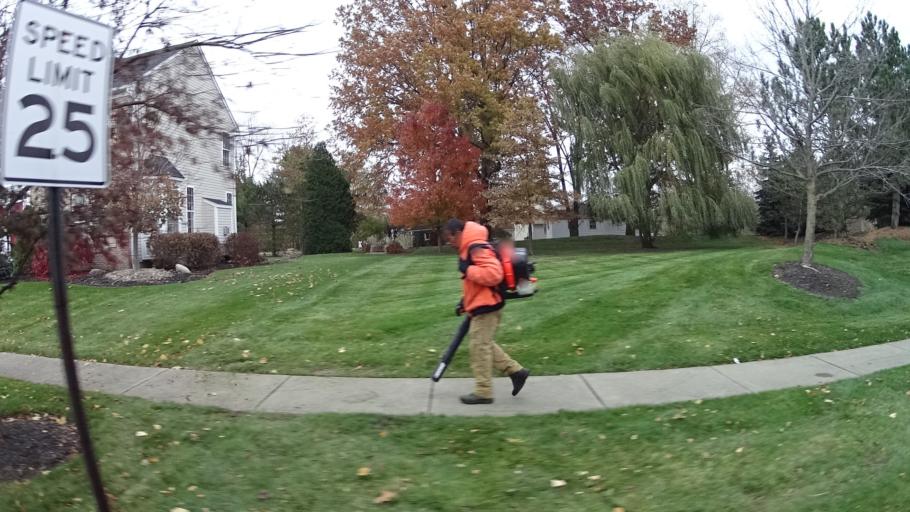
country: US
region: Ohio
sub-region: Lorain County
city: Amherst
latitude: 41.4279
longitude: -82.2265
